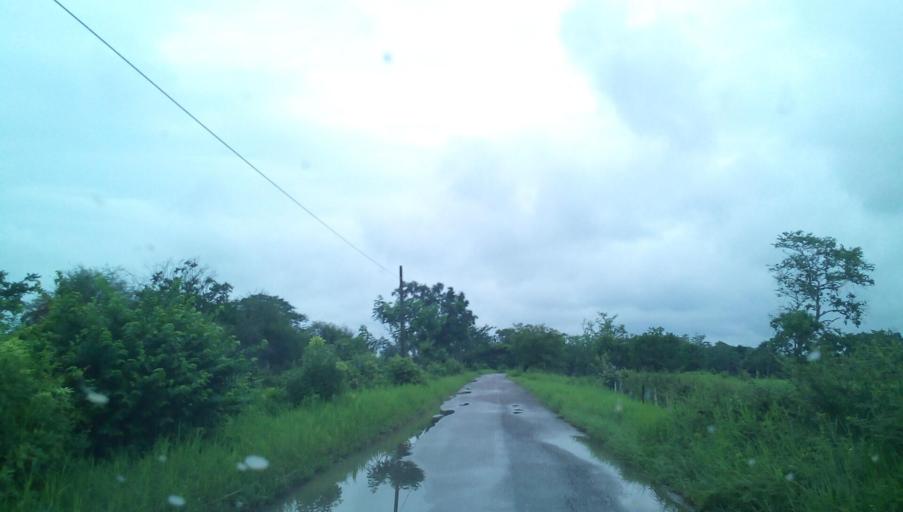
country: MX
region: Veracruz
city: Tempoal de Sanchez
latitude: 21.4803
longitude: -98.4189
